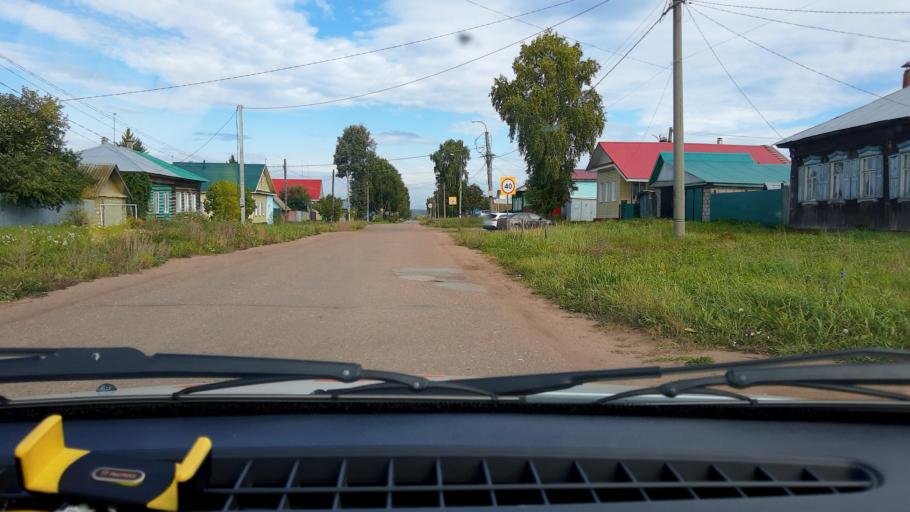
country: RU
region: Bashkortostan
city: Blagoveshchensk
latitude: 55.0297
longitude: 55.9832
